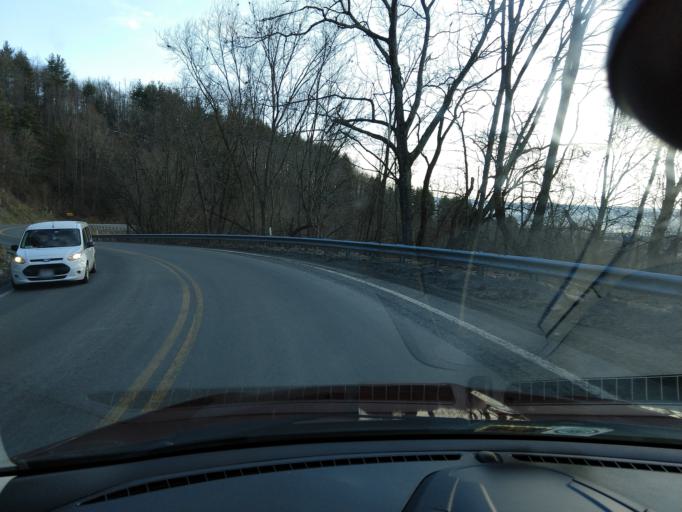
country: US
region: West Virginia
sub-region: Pocahontas County
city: Marlinton
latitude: 38.1164
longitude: -80.2585
